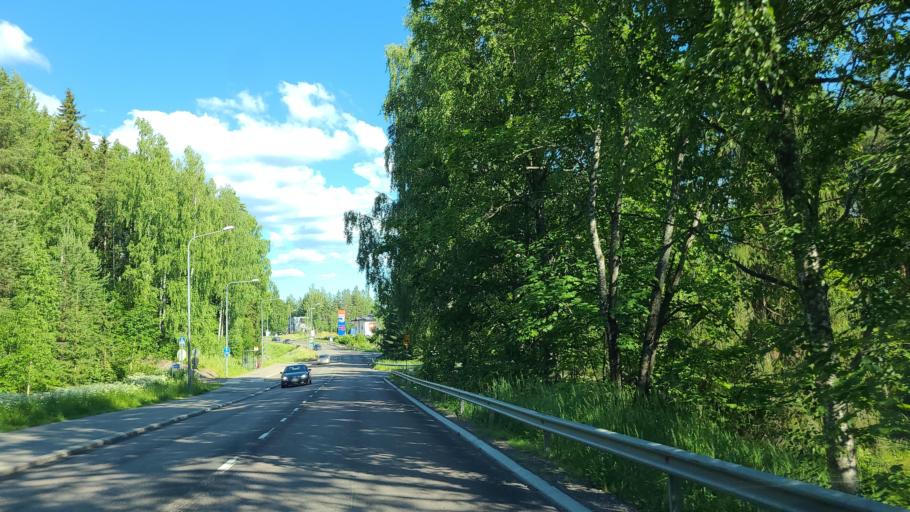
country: FI
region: Central Finland
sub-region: Jyvaeskylae
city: Jyvaeskylae
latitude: 62.2416
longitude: 25.8022
